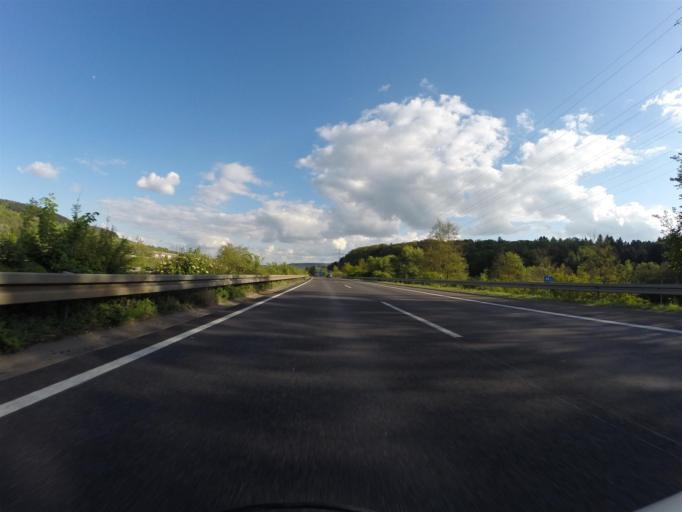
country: DE
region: Saarland
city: Merzig
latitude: 49.4360
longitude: 6.6259
